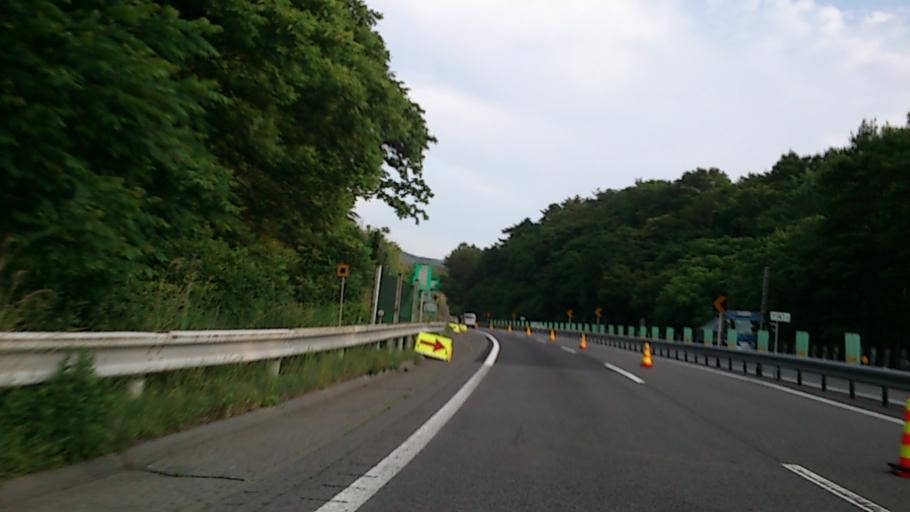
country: JP
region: Nagano
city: Tatsuno
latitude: 35.9872
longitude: 138.0062
